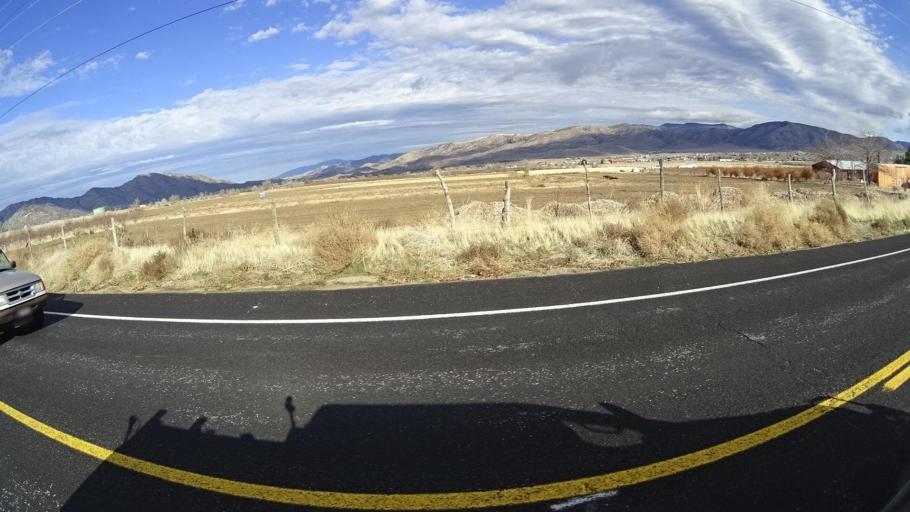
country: US
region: California
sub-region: Kern County
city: Tehachapi
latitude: 35.1094
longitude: -118.4740
